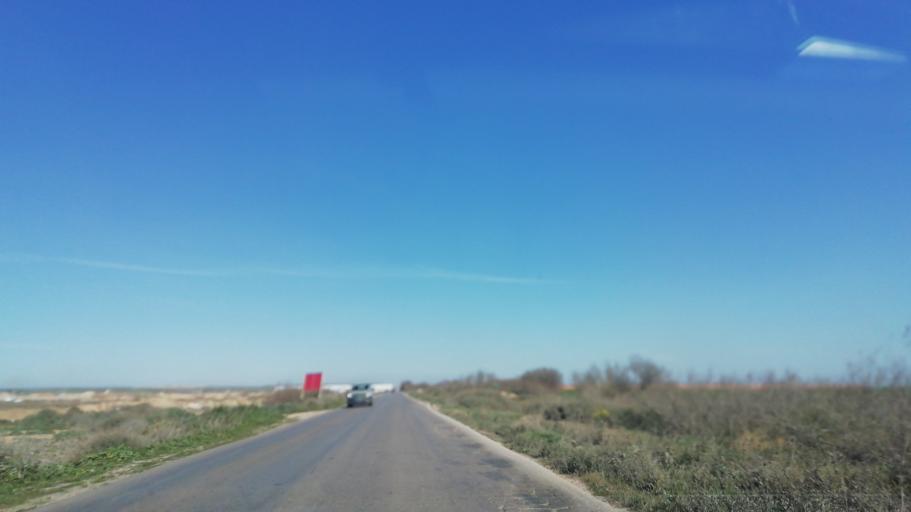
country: DZ
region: Oran
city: Es Senia
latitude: 35.4983
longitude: -0.5962
